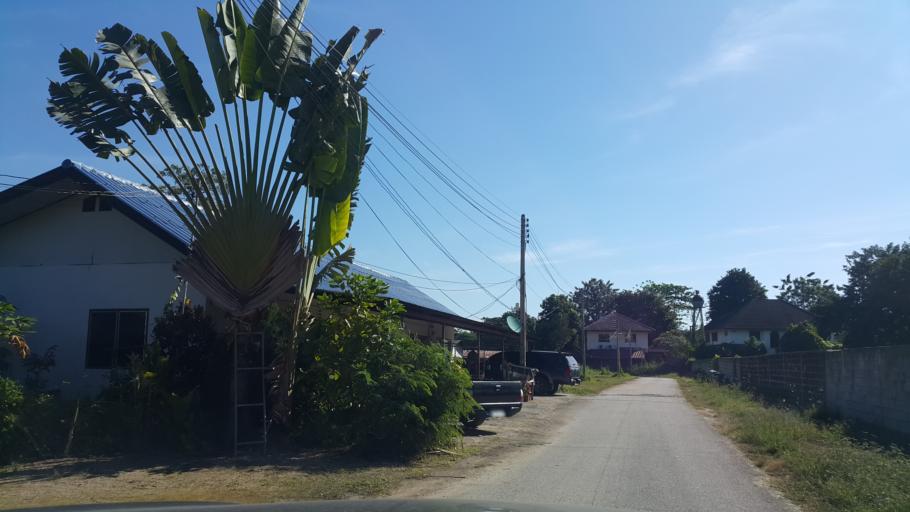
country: TH
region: Chiang Mai
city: San Sai
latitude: 18.8479
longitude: 98.9977
